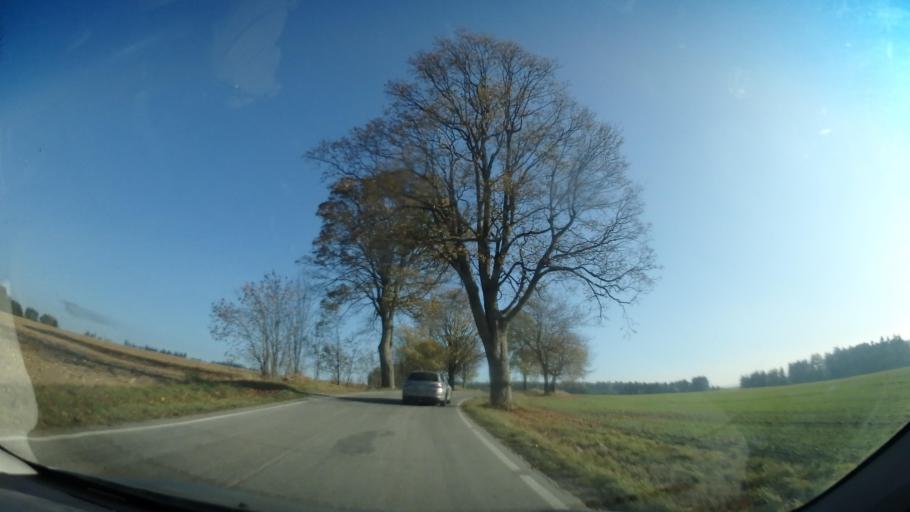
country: CZ
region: Vysocina
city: Zd'ar nad Sazavou Druhy
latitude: 49.6112
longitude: 15.9252
